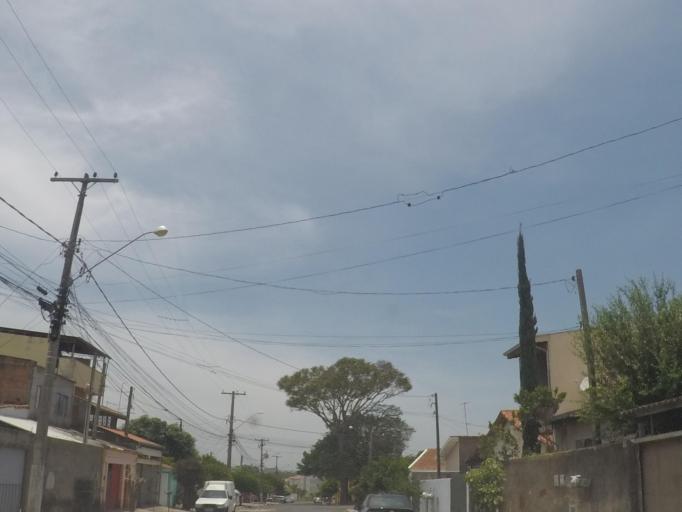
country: BR
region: Sao Paulo
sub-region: Hortolandia
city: Hortolandia
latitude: -22.8467
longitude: -47.1899
